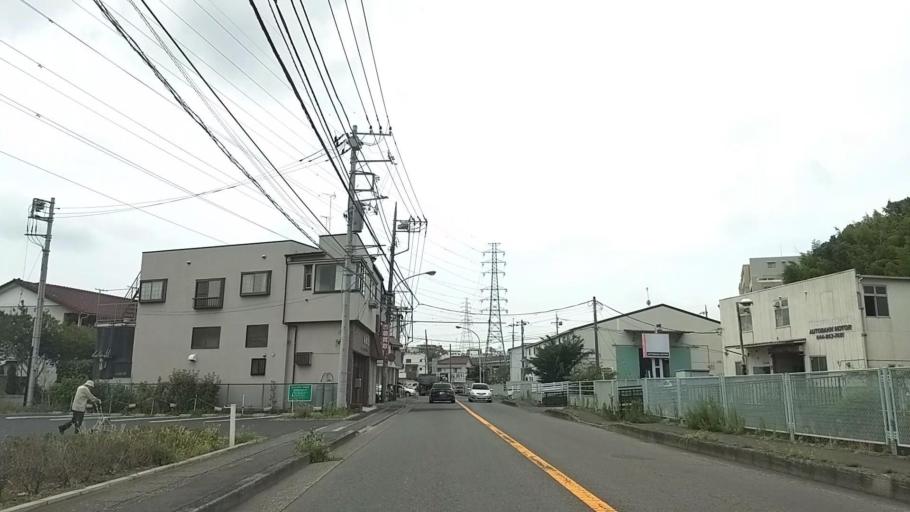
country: JP
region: Kanagawa
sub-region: Kawasaki-shi
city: Kawasaki
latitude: 35.5660
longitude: 139.6133
